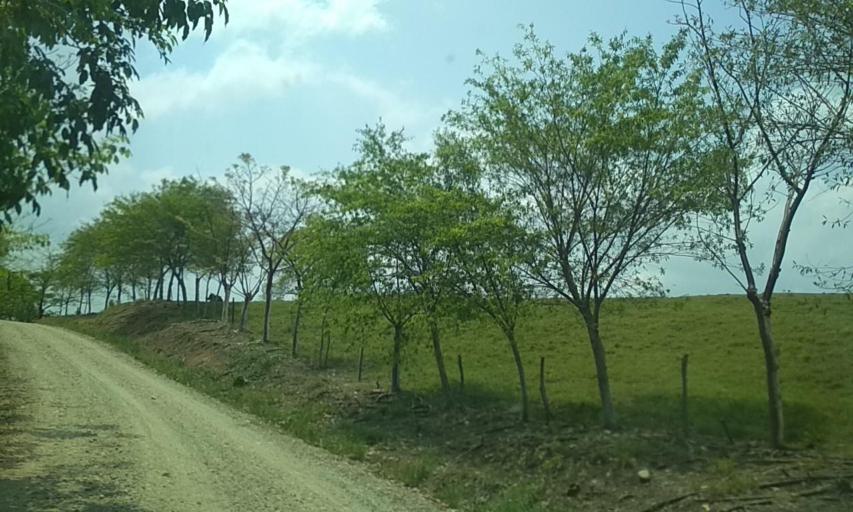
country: MX
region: Tabasco
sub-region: Huimanguillo
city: Francisco Rueda
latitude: 17.6222
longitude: -93.8166
